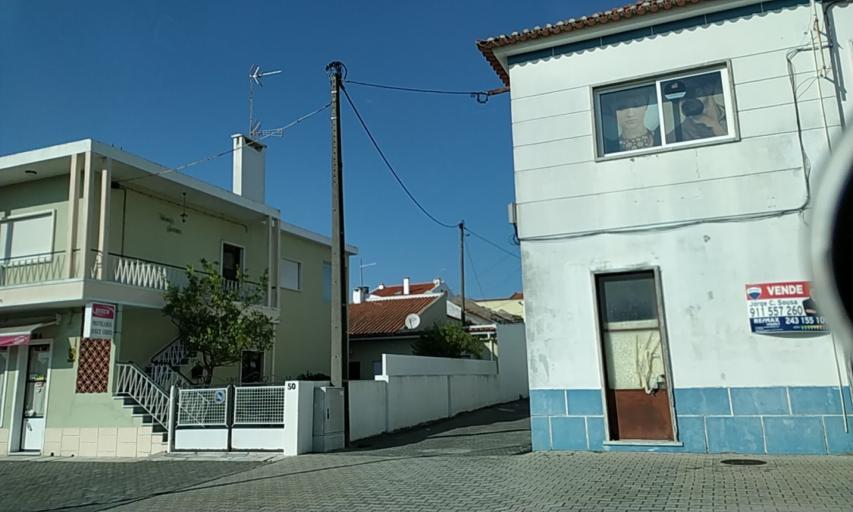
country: PT
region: Santarem
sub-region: Coruche
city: Coruche
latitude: 38.9624
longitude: -8.5310
